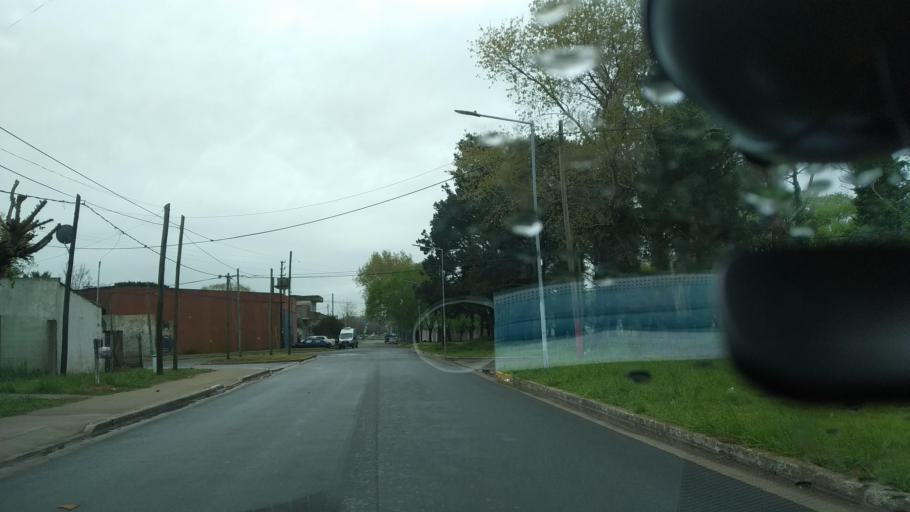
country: AR
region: Buenos Aires
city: Mar del Tuyu
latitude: -36.5357
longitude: -56.7129
